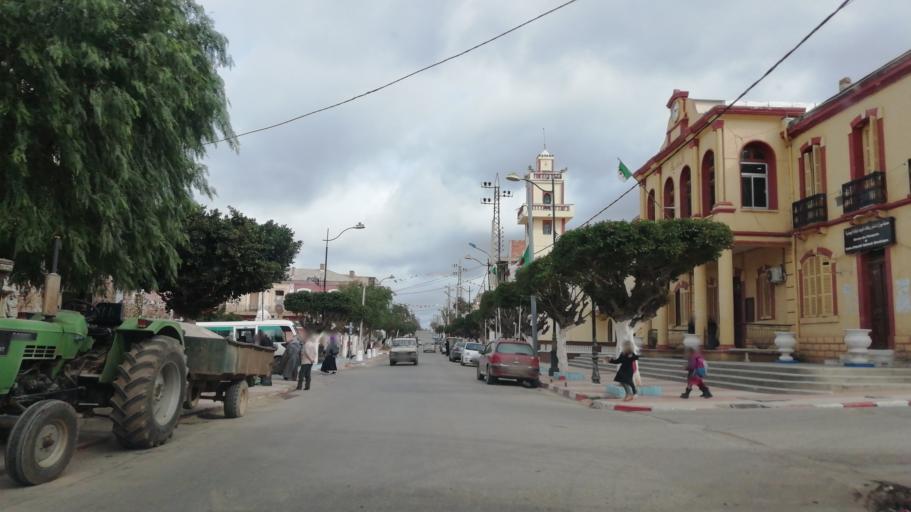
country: DZ
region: Oran
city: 'Ain el Turk
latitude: 35.6862
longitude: -0.8692
